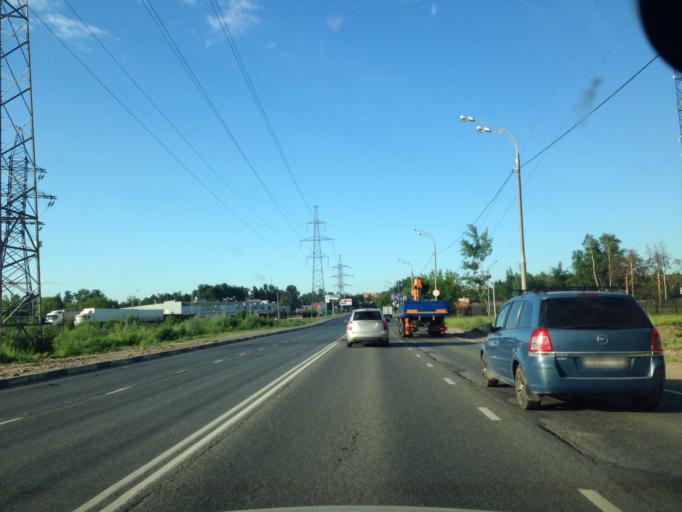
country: RU
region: Moscow
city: Vostochnyy
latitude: 55.7946
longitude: 37.8958
